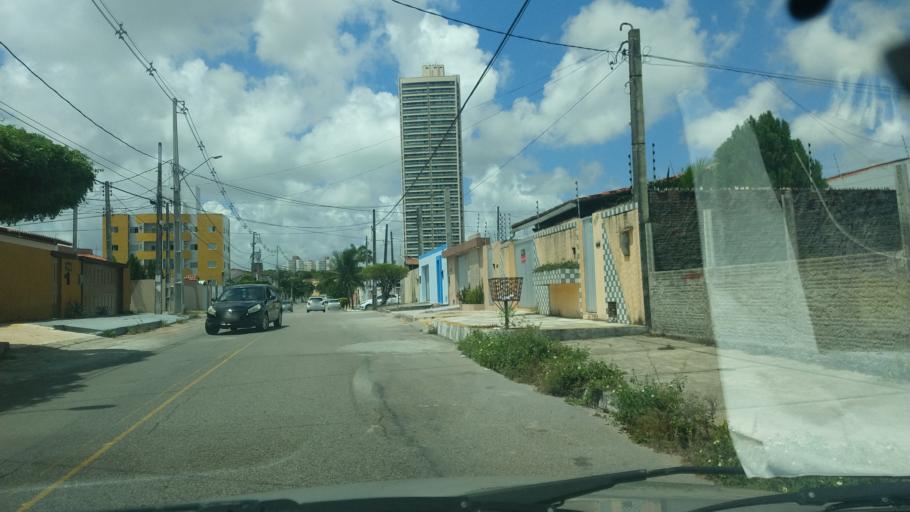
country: BR
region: Rio Grande do Norte
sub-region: Natal
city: Natal
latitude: -5.8680
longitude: -35.1920
